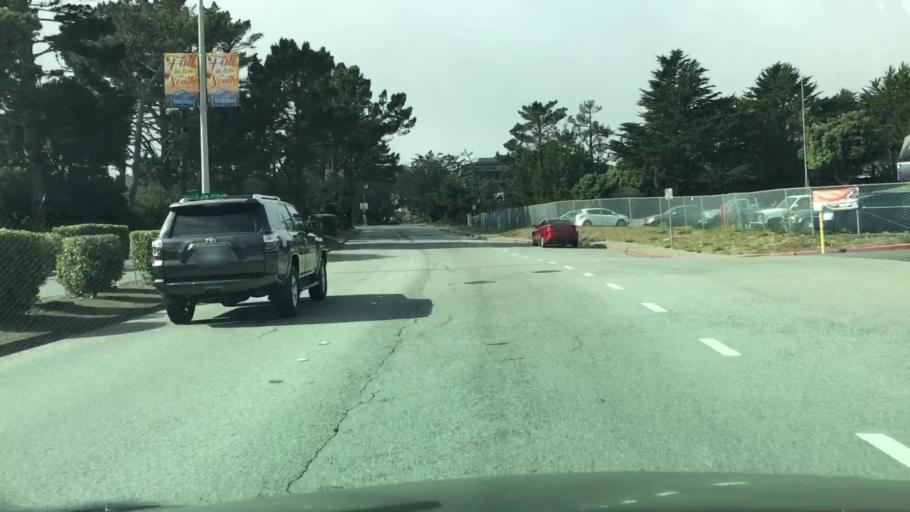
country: US
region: California
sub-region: San Mateo County
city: Colma
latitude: 37.6434
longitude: -122.4602
